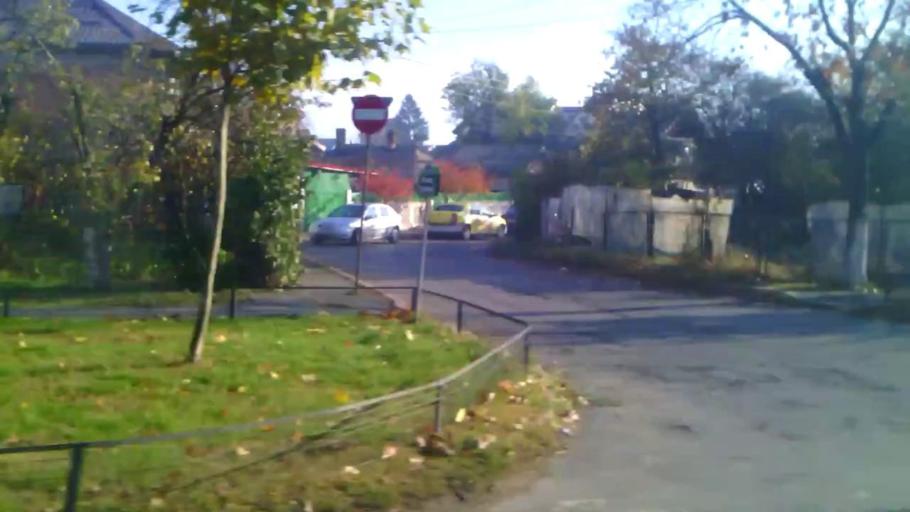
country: RO
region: Ilfov
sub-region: Comuna Popesti-Leordeni
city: Popesti-Leordeni
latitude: 44.3732
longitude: 26.1399
